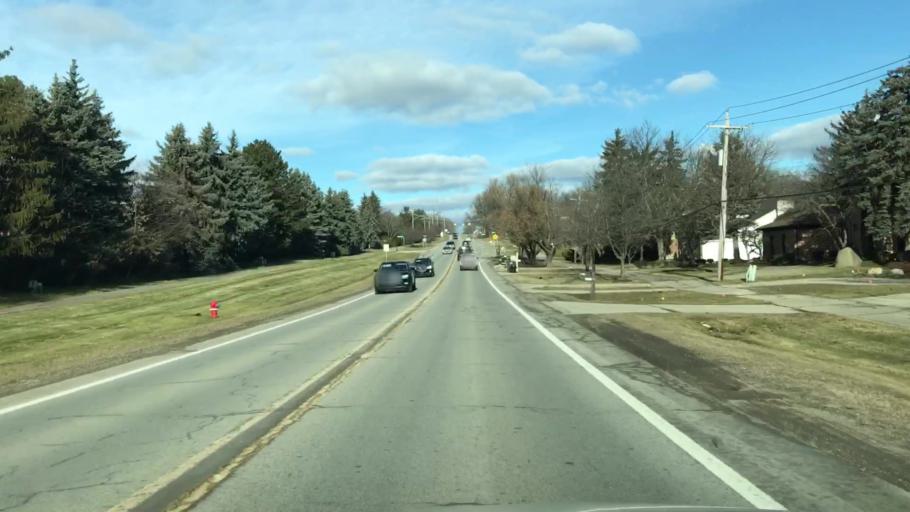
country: US
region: Michigan
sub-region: Oakland County
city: Auburn Hills
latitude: 42.7058
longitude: -83.1951
